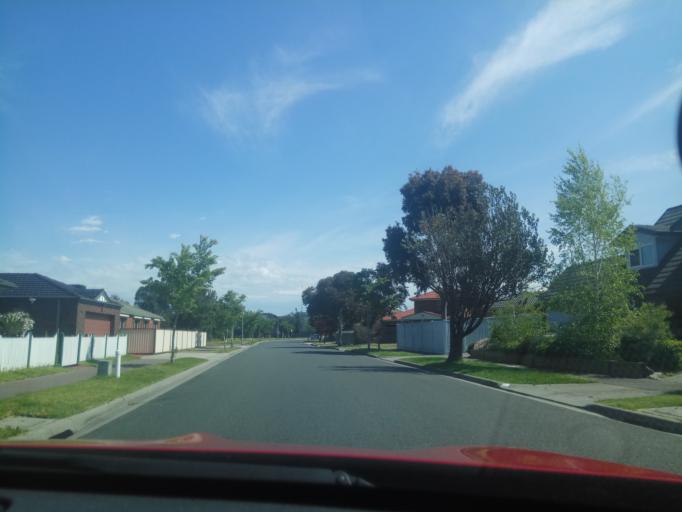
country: AU
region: Victoria
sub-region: Kingston
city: Aspendale Gardens
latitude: -38.0224
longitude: 145.1207
